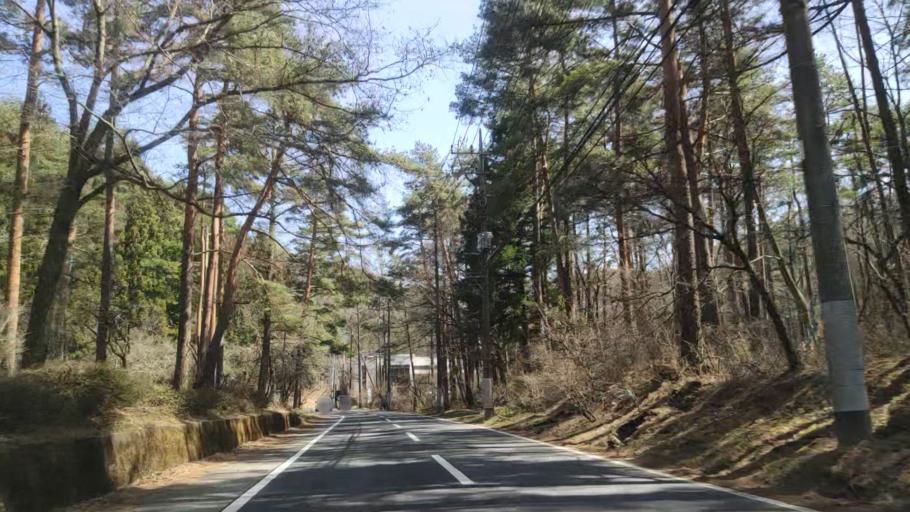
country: JP
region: Yamanashi
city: Fujikawaguchiko
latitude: 35.4642
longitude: 138.8148
